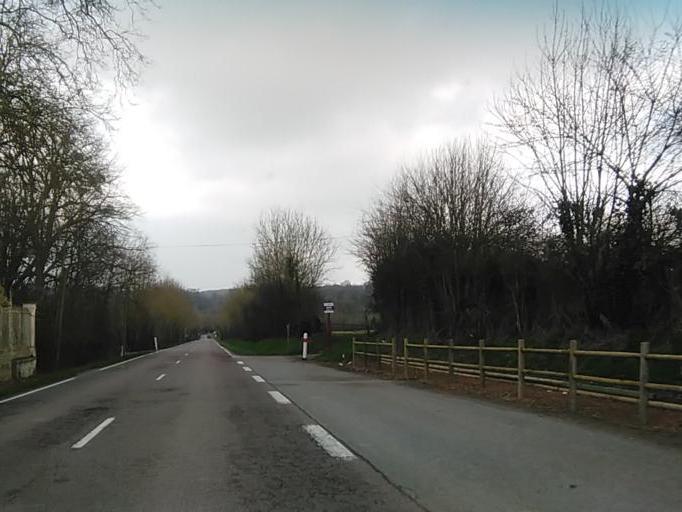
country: FR
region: Lower Normandy
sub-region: Departement du Calvados
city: Falaise
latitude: 48.8418
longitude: -0.2334
